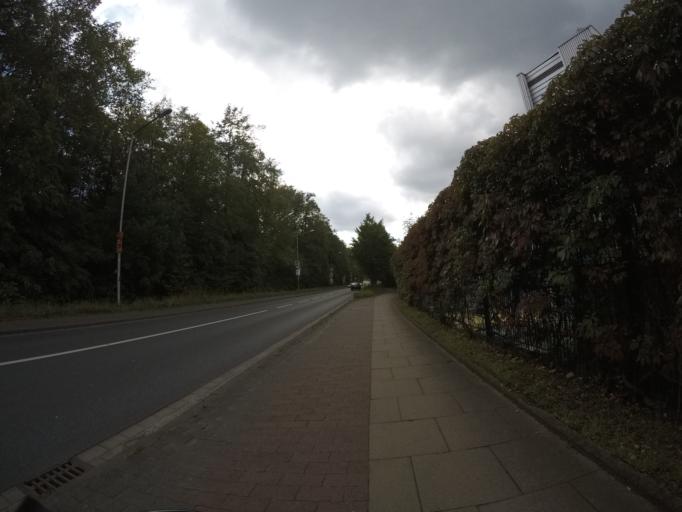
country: DE
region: North Rhine-Westphalia
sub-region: Regierungsbezirk Detmold
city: Herford
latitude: 52.1277
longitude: 8.6665
